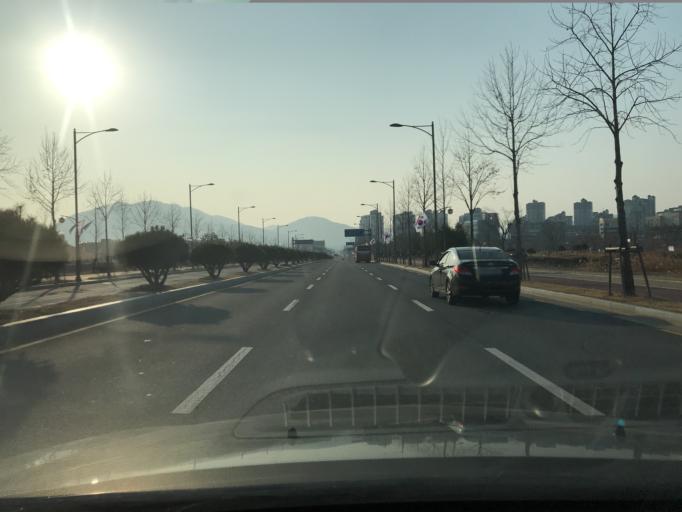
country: KR
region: Daegu
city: Hwawon
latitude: 35.6892
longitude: 128.4620
